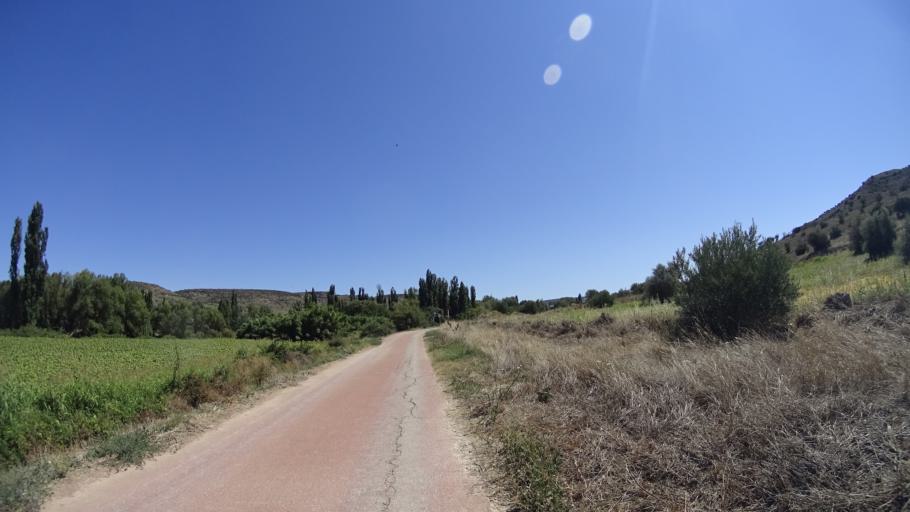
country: ES
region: Madrid
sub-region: Provincia de Madrid
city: Tielmes
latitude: 40.2425
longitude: -3.2796
